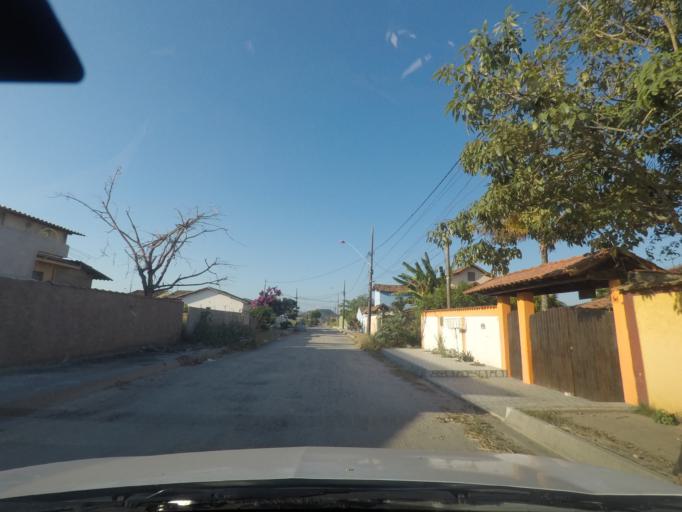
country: BR
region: Rio de Janeiro
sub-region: Marica
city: Marica
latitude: -22.9652
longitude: -42.9352
